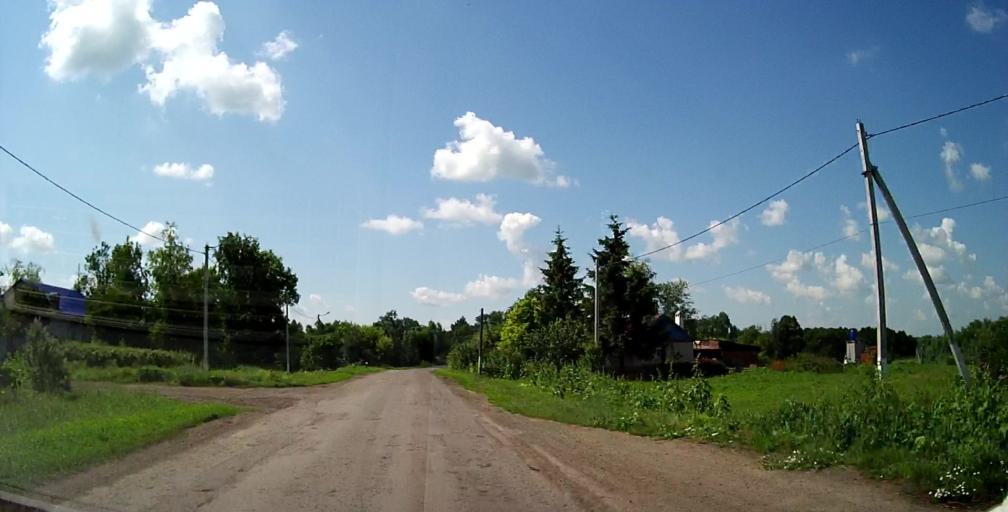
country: RU
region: Lipetsk
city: Chaplygin
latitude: 53.3731
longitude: 39.9170
